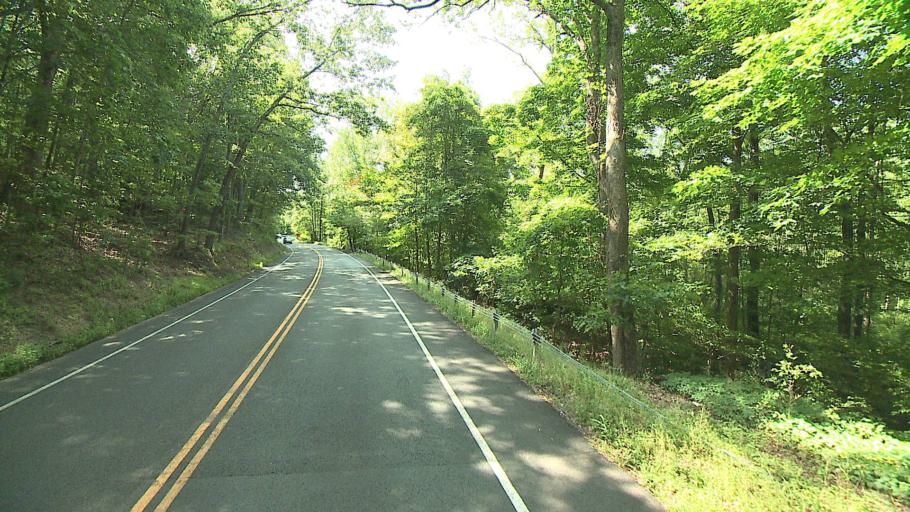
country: US
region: Connecticut
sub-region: Fairfield County
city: Trumbull
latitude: 41.3033
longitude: -73.2848
